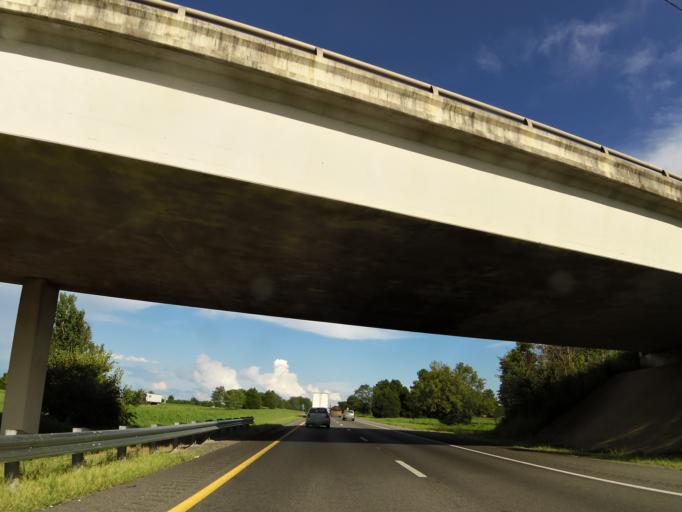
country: US
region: Tennessee
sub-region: Montgomery County
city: Clarksville
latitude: 36.6300
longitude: -87.3173
